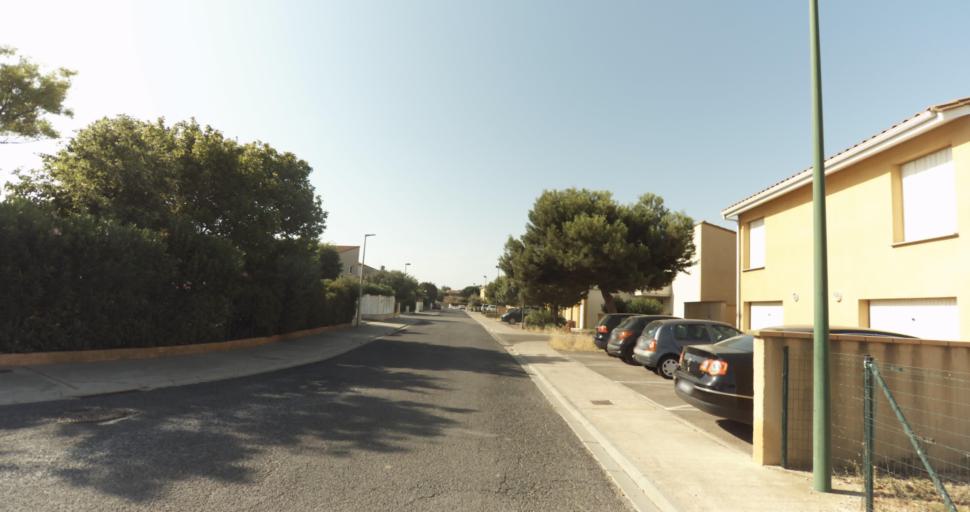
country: FR
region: Languedoc-Roussillon
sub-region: Departement des Pyrenees-Orientales
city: Alenya
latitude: 42.6436
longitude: 2.9781
